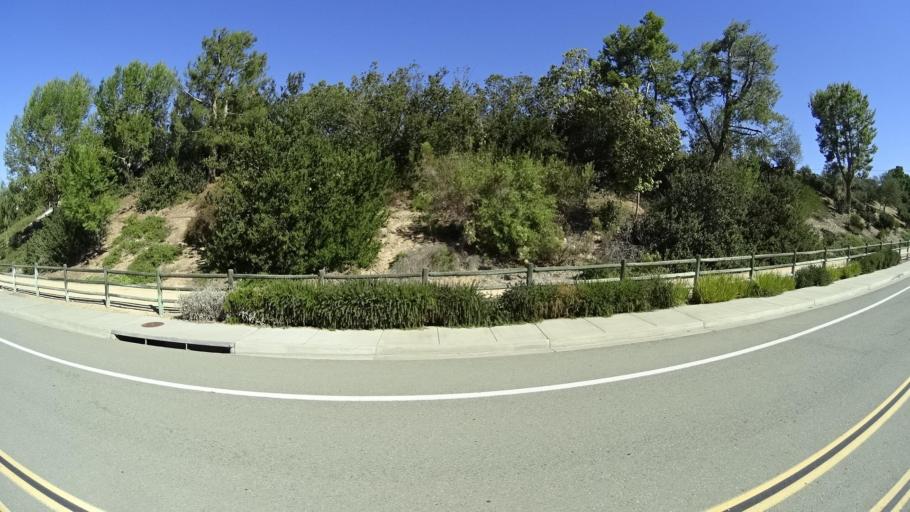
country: US
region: California
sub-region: San Diego County
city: La Presa
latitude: 32.6641
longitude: -116.9785
